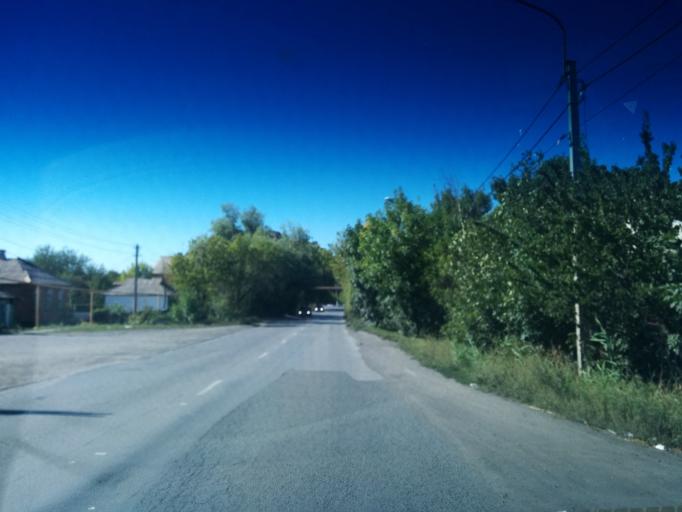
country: RU
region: Rostov
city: Shakhty
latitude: 47.6903
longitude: 40.2608
